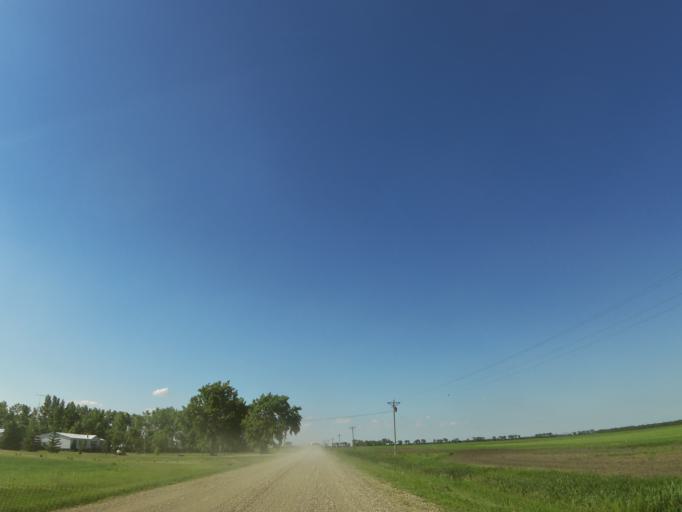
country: US
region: North Dakota
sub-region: Walsh County
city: Grafton
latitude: 48.3183
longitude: -97.2552
